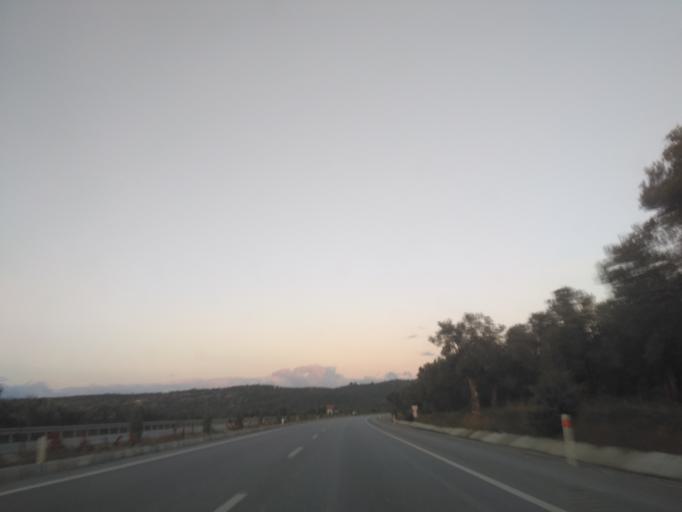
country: TR
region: Balikesir
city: Emrutabat
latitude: 39.4556
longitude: 26.8863
